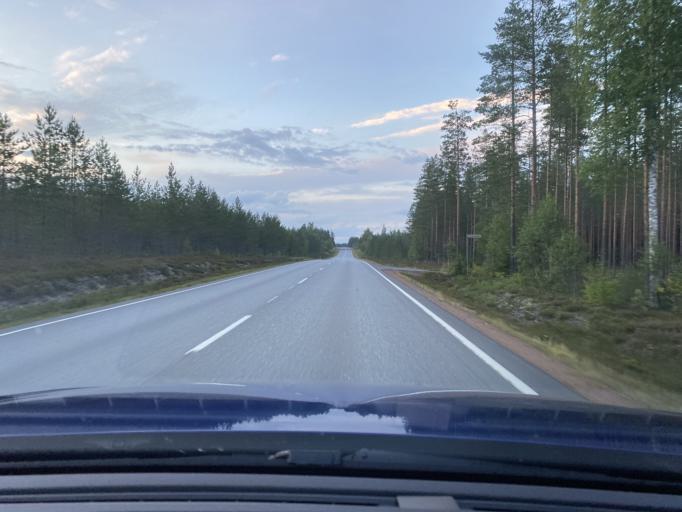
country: FI
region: Satakunta
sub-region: Pohjois-Satakunta
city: Honkajoki
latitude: 62.0280
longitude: 22.2331
